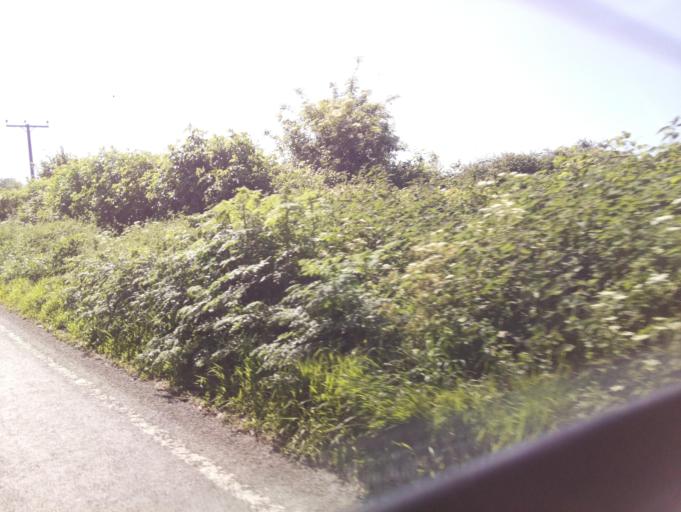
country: GB
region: England
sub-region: Somerset
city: Crewkerne
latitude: 50.8918
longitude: -2.7763
